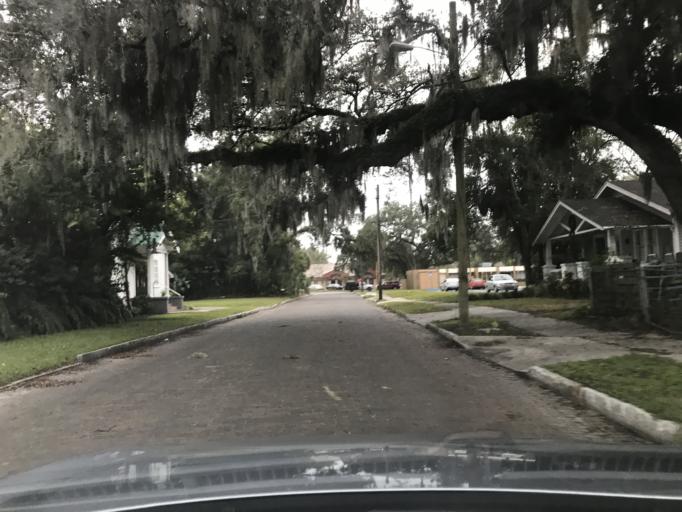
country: US
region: Florida
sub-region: Hillsborough County
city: Tampa
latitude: 27.9825
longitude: -82.4653
